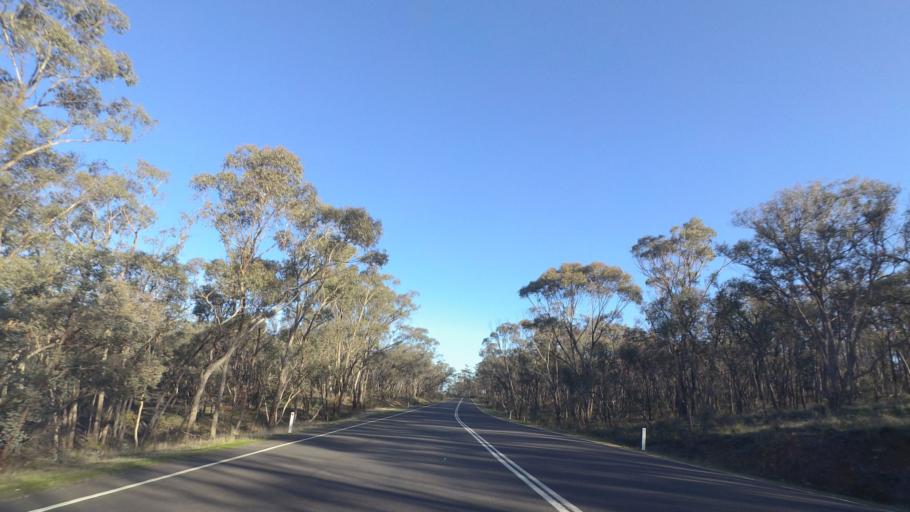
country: AU
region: Victoria
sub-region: Greater Bendigo
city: Kennington
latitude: -36.9108
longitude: 144.4931
